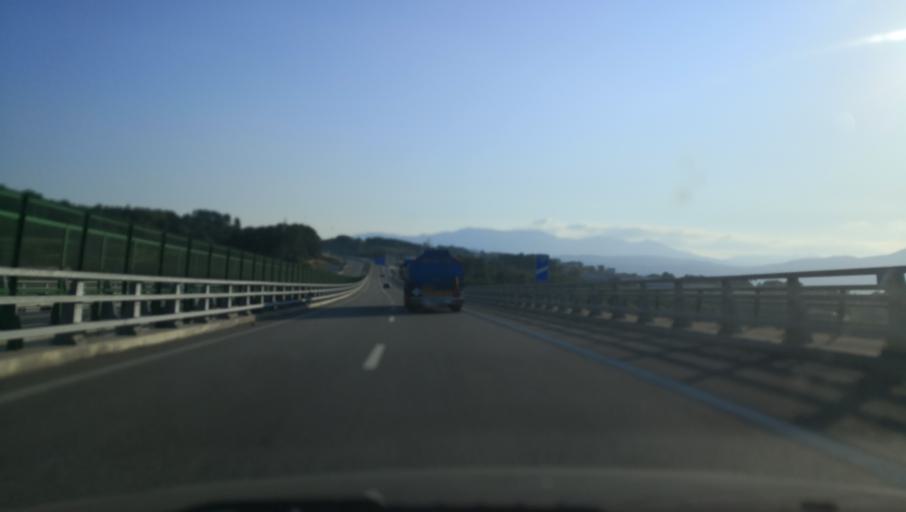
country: PT
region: Vila Real
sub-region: Vila Real
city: Vila Real
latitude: 41.2843
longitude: -7.7131
